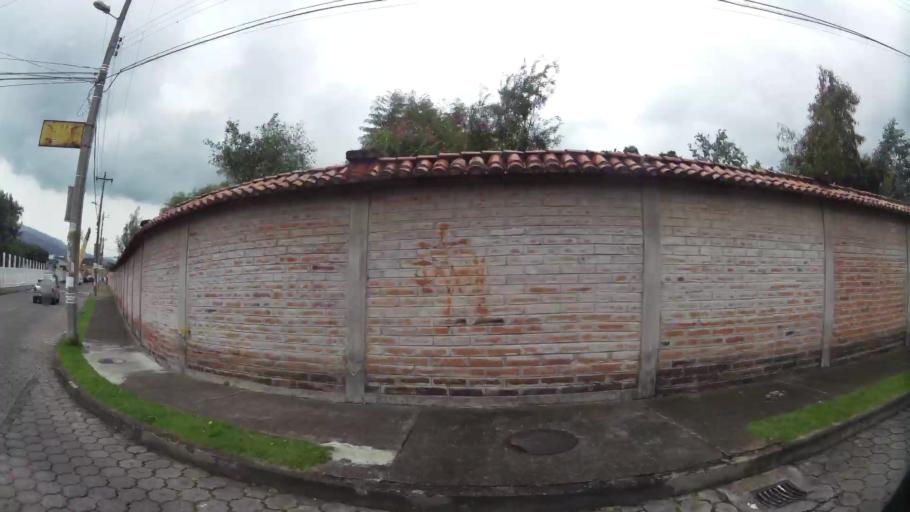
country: EC
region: Pichincha
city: Sangolqui
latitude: -0.3102
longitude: -78.4634
